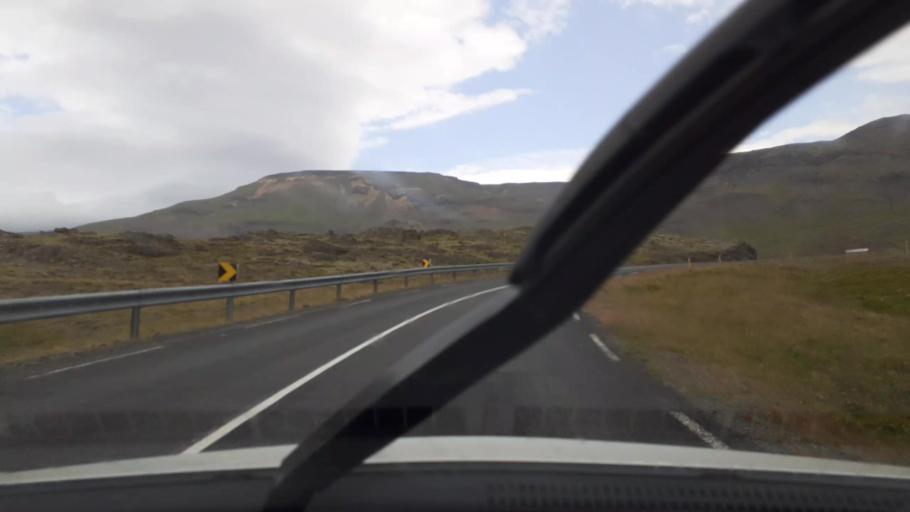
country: IS
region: Capital Region
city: Mosfellsbaer
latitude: 64.3932
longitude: -21.4353
